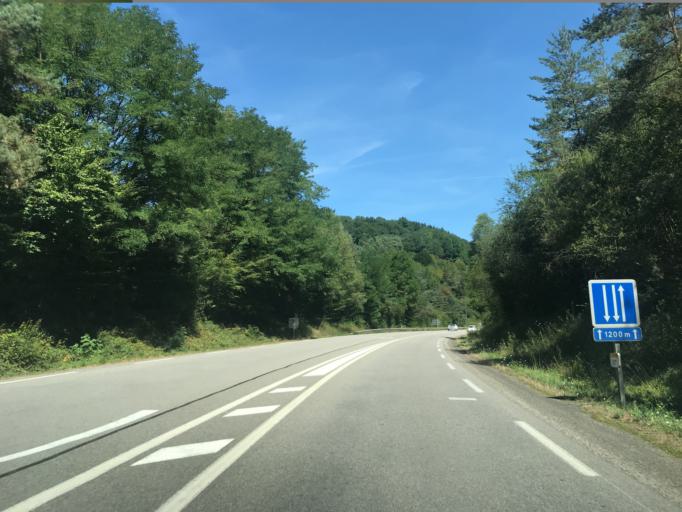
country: FR
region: Limousin
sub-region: Departement de la Correze
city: Laguenne
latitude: 45.2547
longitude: 1.7767
